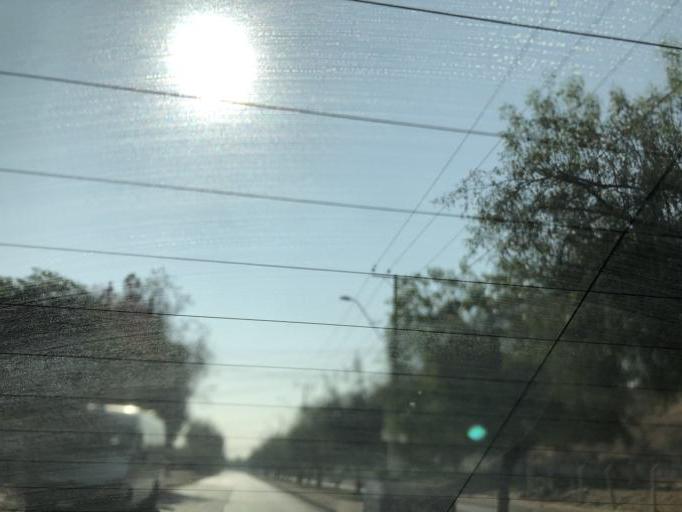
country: CL
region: Santiago Metropolitan
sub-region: Provincia de Cordillera
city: Puente Alto
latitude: -33.5997
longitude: -70.5566
